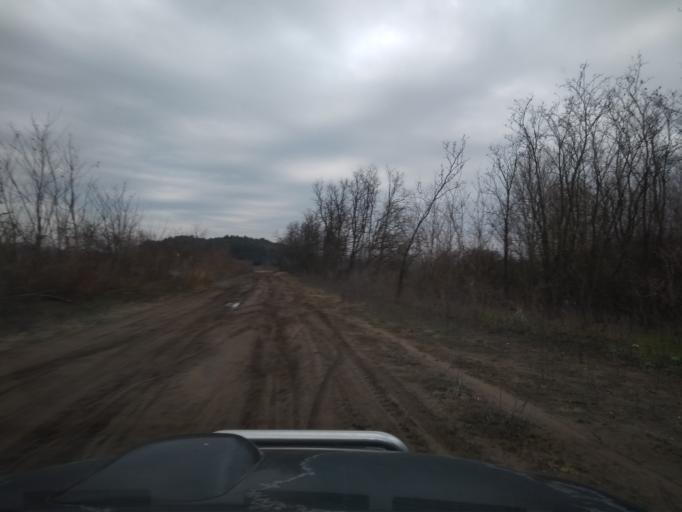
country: HU
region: Szabolcs-Szatmar-Bereg
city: Nyirpazony
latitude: 47.9933
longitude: 21.7883
